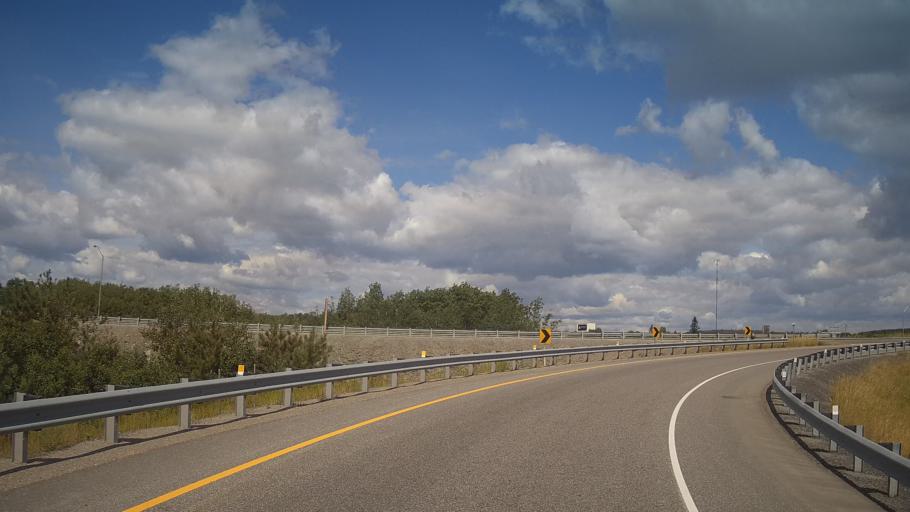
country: CA
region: Ontario
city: Greater Sudbury
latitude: 46.4261
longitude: -81.1216
